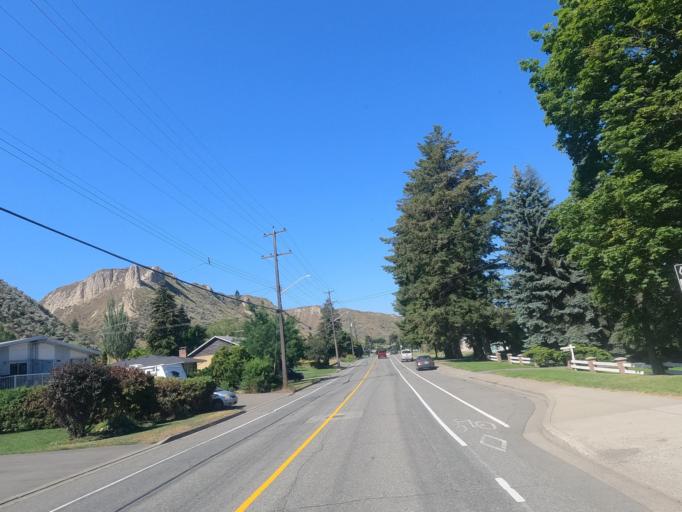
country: CA
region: British Columbia
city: Kamloops
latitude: 50.6762
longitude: -120.2661
